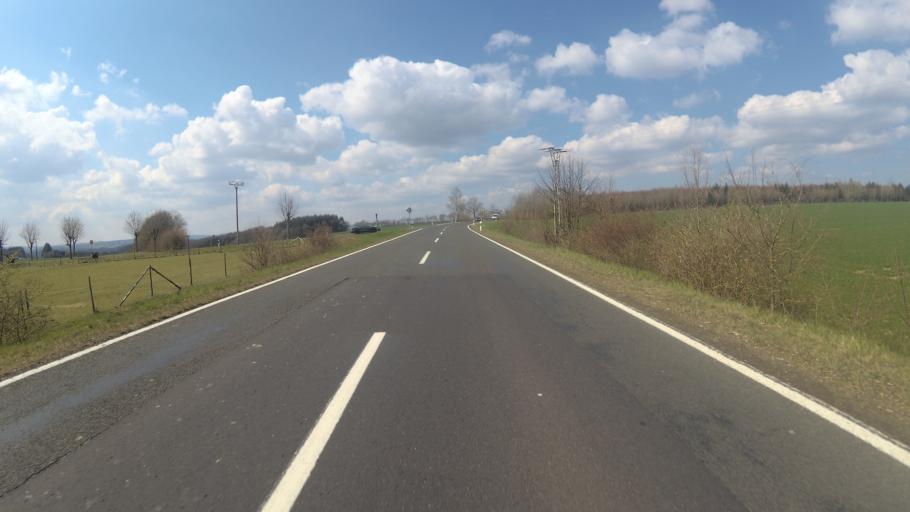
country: DE
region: Rheinland-Pfalz
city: Brockscheid
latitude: 50.1359
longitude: 6.8482
